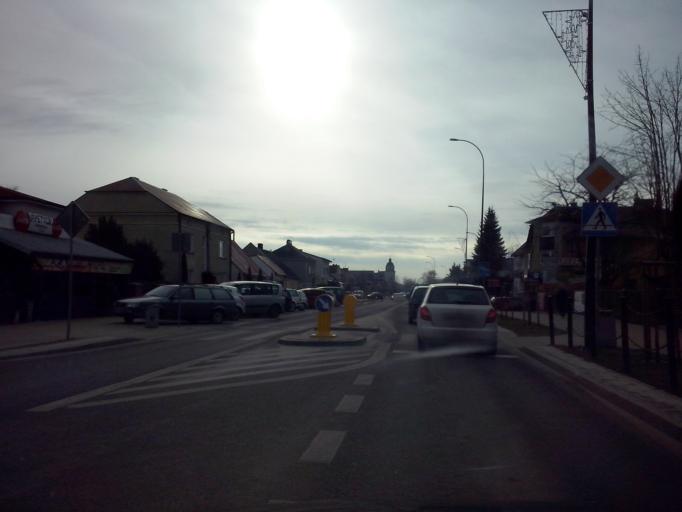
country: PL
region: Lublin Voivodeship
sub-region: Powiat bilgorajski
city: Bilgoraj
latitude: 50.5296
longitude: 22.7161
